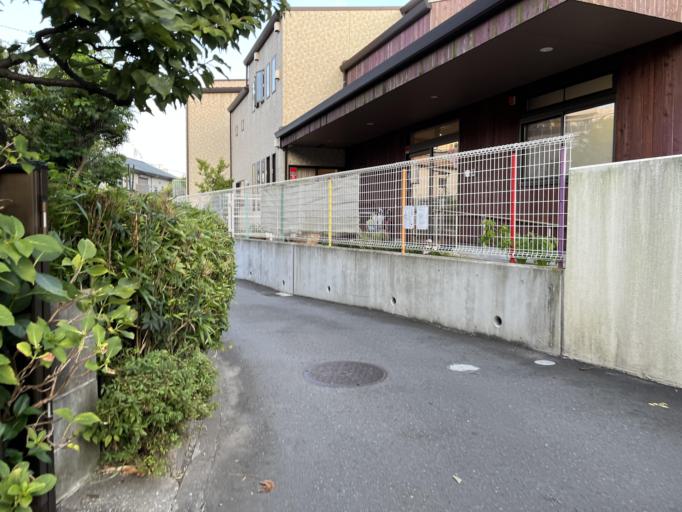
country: JP
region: Kanagawa
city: Yokohama
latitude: 35.3942
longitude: 139.6098
